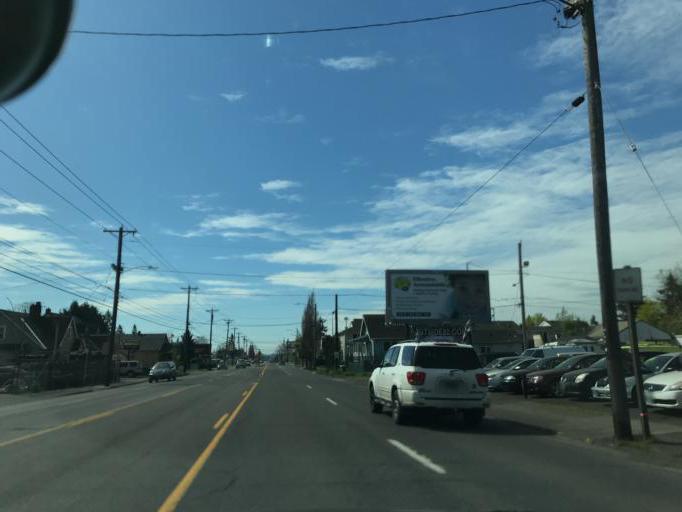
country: US
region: Oregon
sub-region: Multnomah County
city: Lents
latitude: 45.4749
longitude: -122.5792
